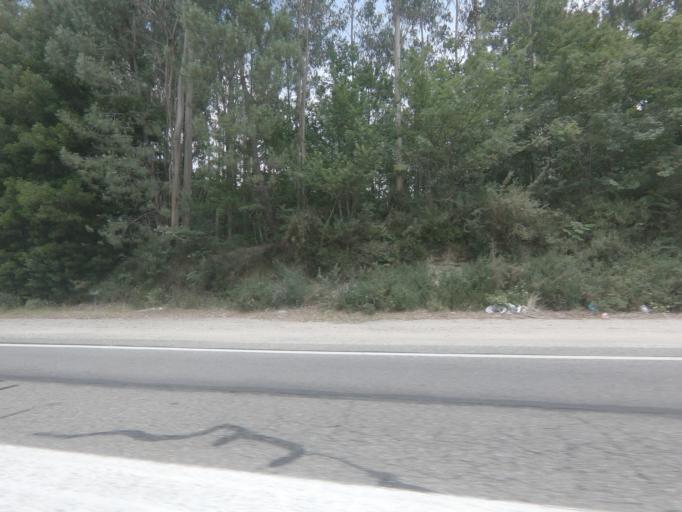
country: ES
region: Galicia
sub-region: Provincia de Pontevedra
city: Tomino
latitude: 42.0185
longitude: -8.7324
